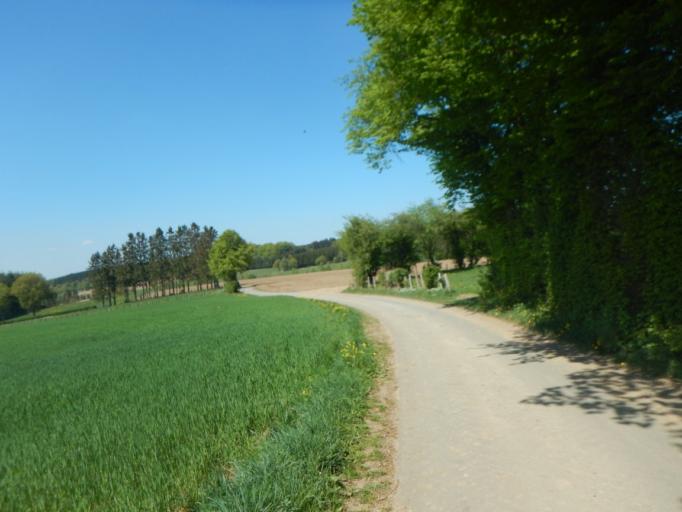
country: LU
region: Diekirch
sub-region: Canton de Clervaux
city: Troisvierges
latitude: 50.1473
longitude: 6.0257
